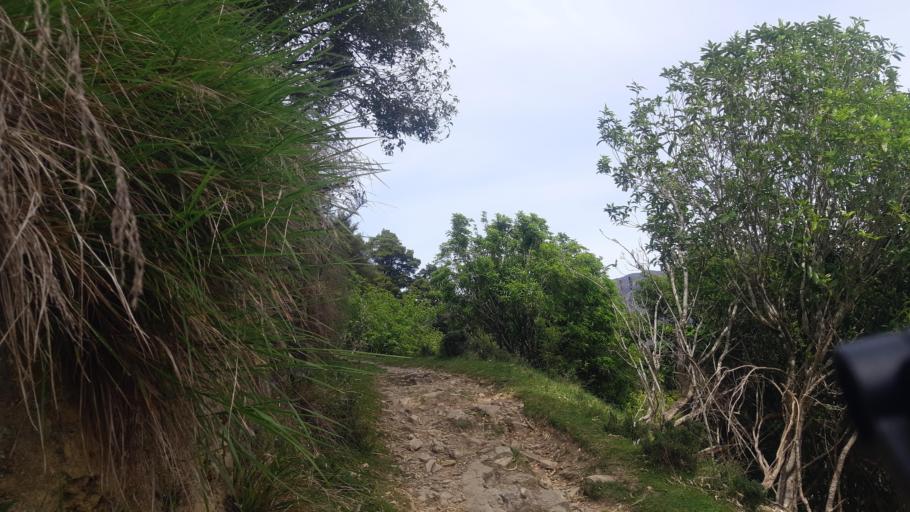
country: NZ
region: Marlborough
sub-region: Marlborough District
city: Picton
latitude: -41.2481
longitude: 173.9586
